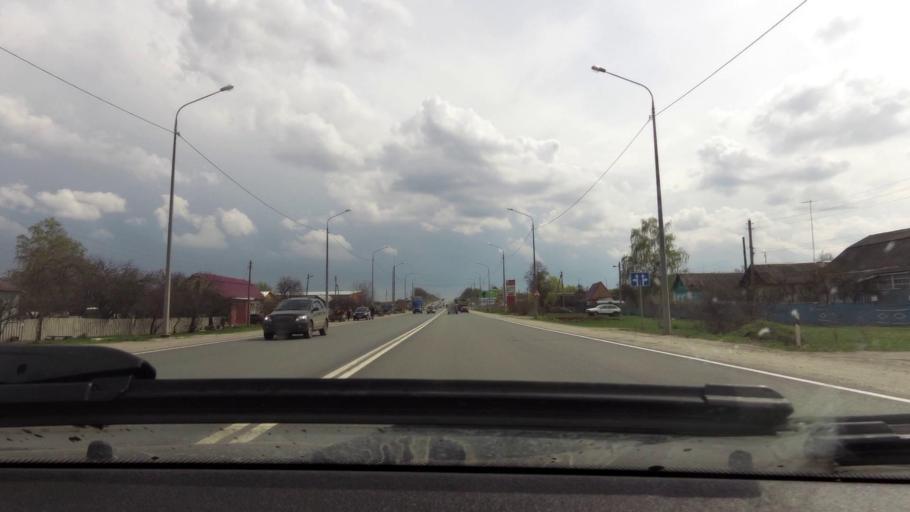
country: RU
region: Rjazan
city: Bagramovo
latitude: 54.7308
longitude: 39.4628
